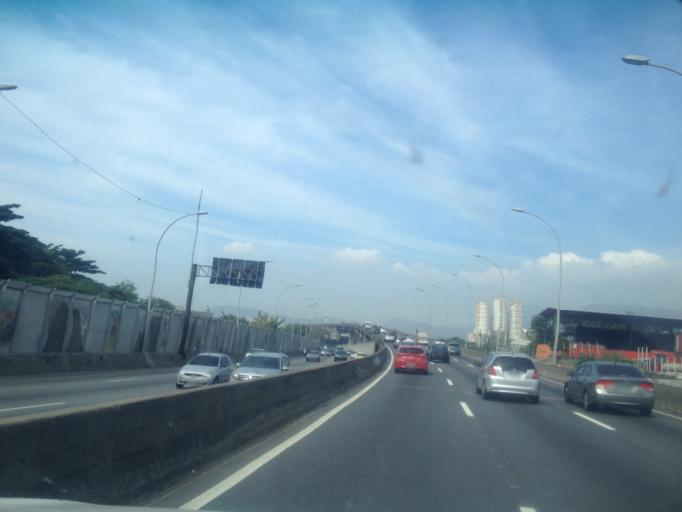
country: BR
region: Rio de Janeiro
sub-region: Rio De Janeiro
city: Rio de Janeiro
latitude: -22.8793
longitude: -43.2319
